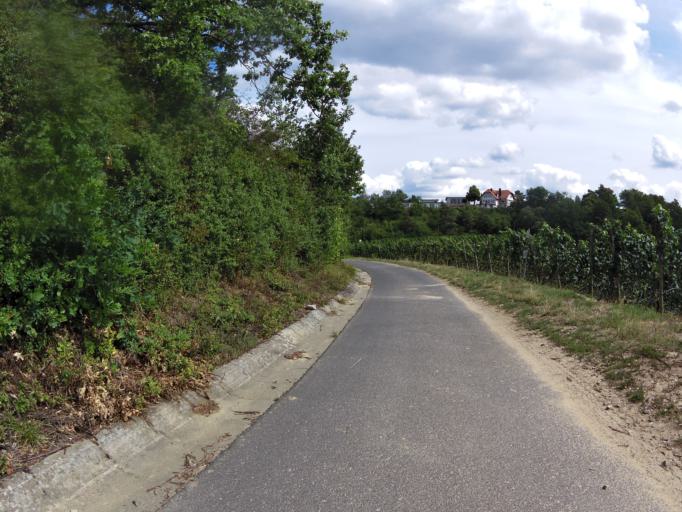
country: DE
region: Bavaria
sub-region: Regierungsbezirk Unterfranken
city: Sommerhausen
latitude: 49.7024
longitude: 10.0320
